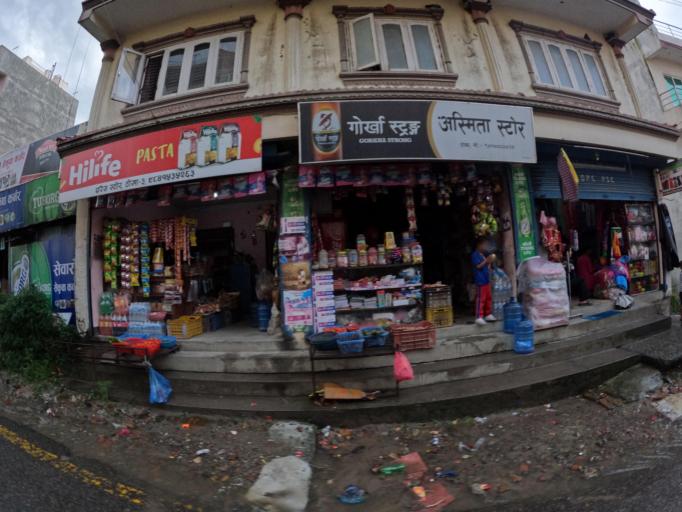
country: NP
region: Central Region
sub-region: Bagmati Zone
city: Kathmandu
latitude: 27.7640
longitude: 85.3306
